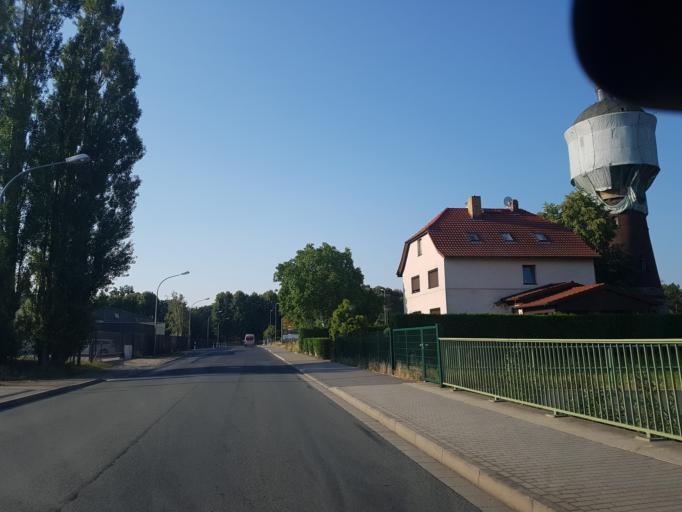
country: DE
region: Brandenburg
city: Elsterwerda
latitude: 51.4557
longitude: 13.5184
